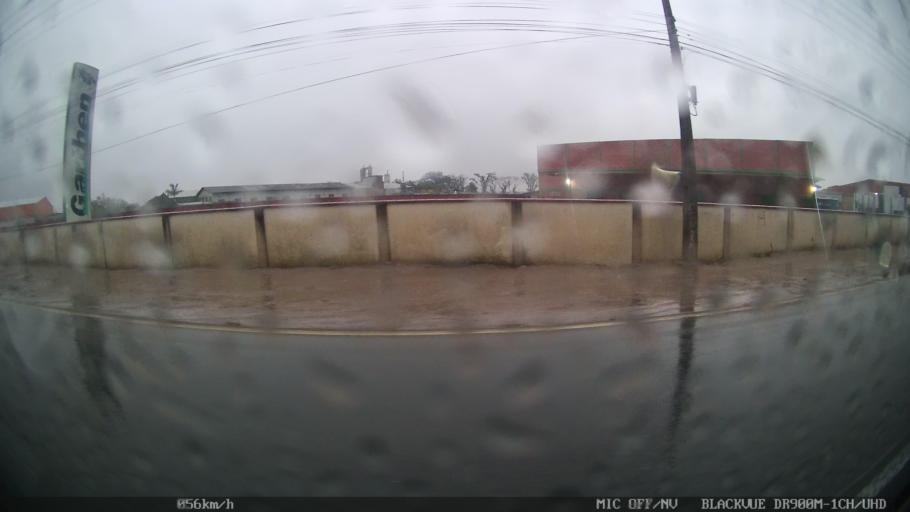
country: BR
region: Santa Catarina
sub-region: Navegantes
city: Navegantes
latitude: -26.8650
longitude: -48.6785
